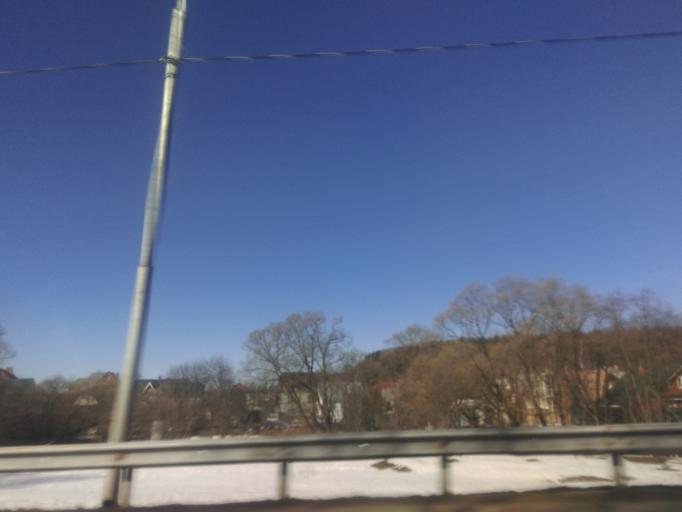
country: RU
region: Moskovskaya
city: Kommunarka
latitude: 55.5393
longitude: 37.4455
